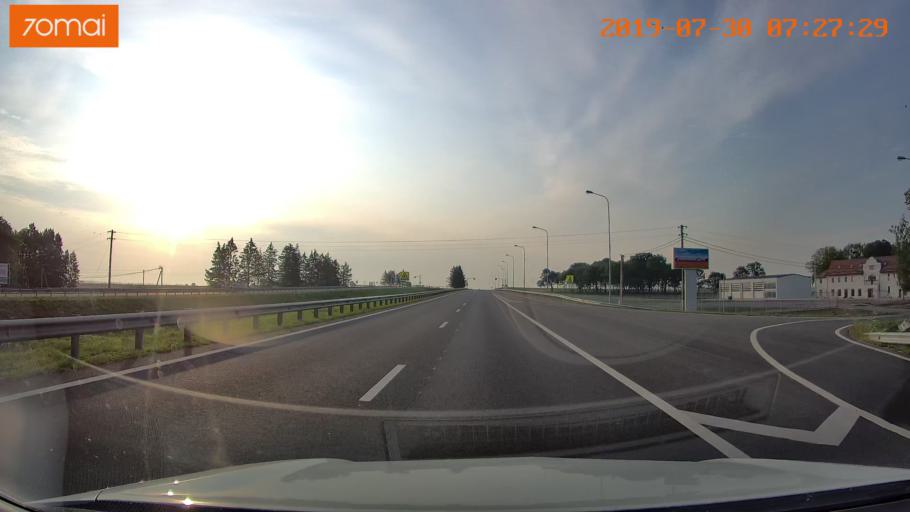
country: RU
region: Kaliningrad
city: Gvardeysk
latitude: 54.6819
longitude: 20.8887
